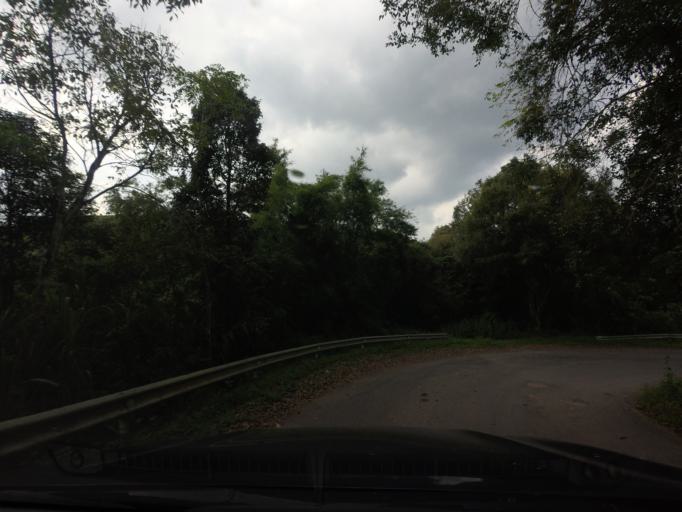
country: TH
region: Nan
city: Bo Kluea
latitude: 19.2685
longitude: 101.1772
